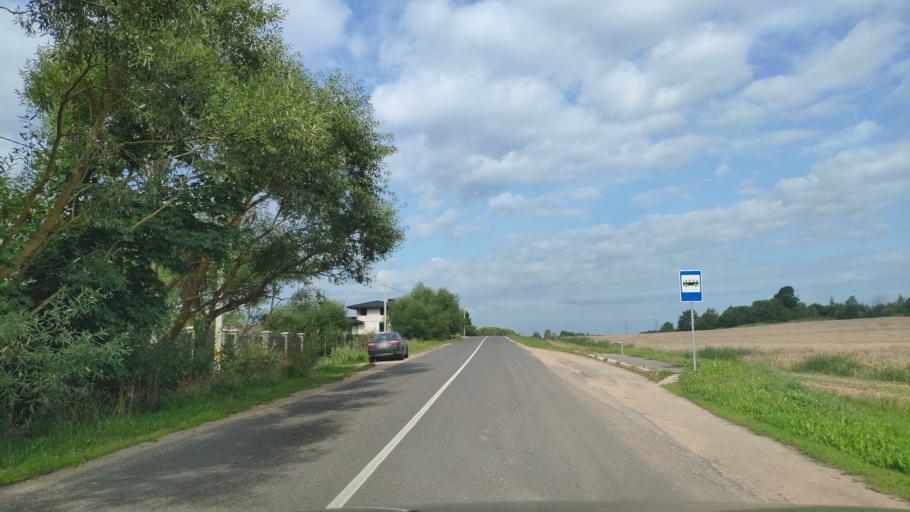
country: BY
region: Minsk
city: Khatsyezhyna
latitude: 53.8693
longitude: 27.3178
